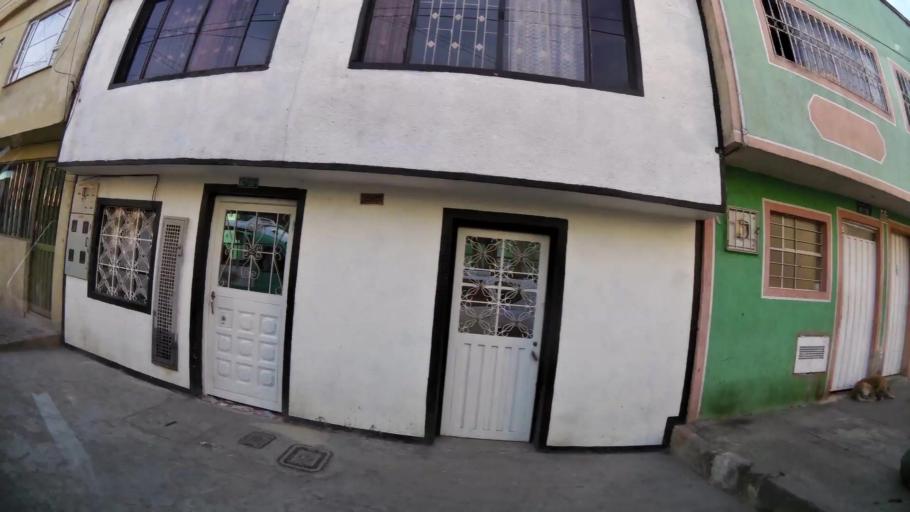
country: CO
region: Bogota D.C.
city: Bogota
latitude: 4.5450
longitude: -74.0988
